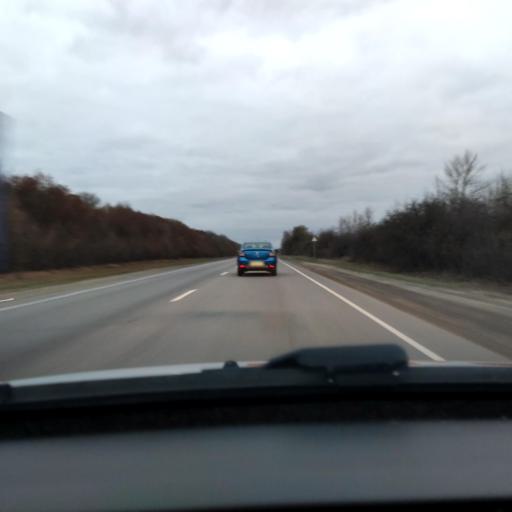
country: RU
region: Lipetsk
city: Borinskoye
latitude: 52.4292
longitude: 39.2648
